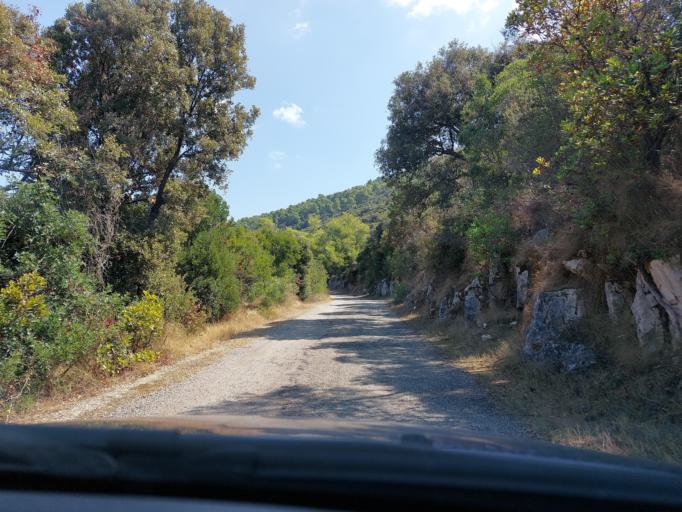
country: HR
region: Dubrovacko-Neretvanska
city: Smokvica
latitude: 42.7674
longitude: 16.8296
